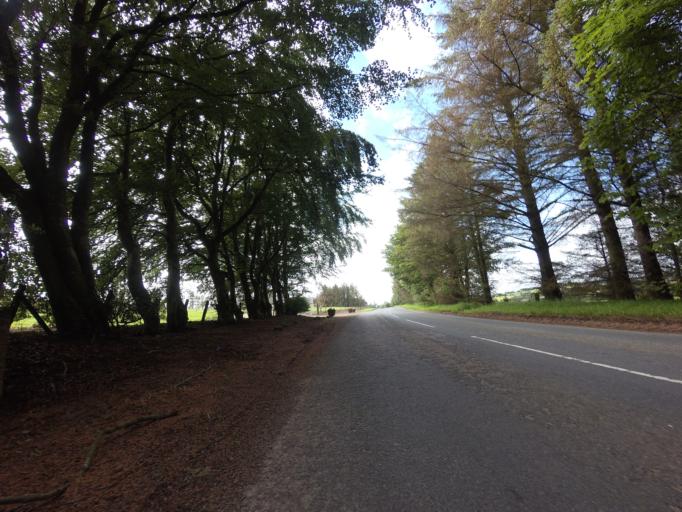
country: GB
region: Scotland
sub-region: Aberdeenshire
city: Turriff
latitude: 57.5432
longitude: -2.3163
